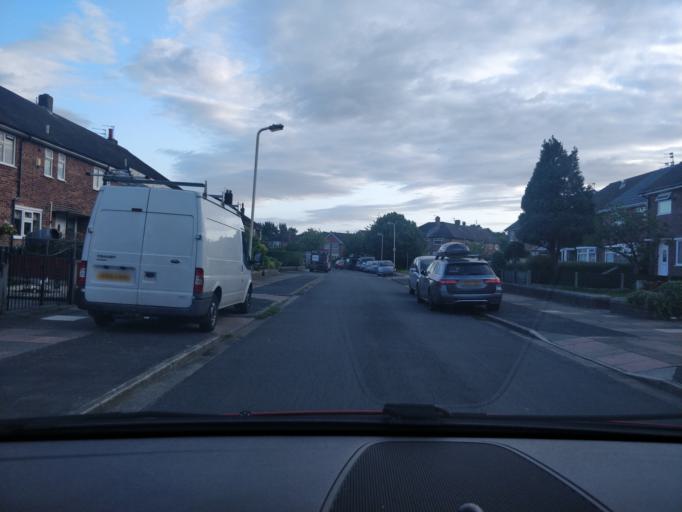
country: GB
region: England
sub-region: Sefton
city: Southport
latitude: 53.6636
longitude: -2.9774
